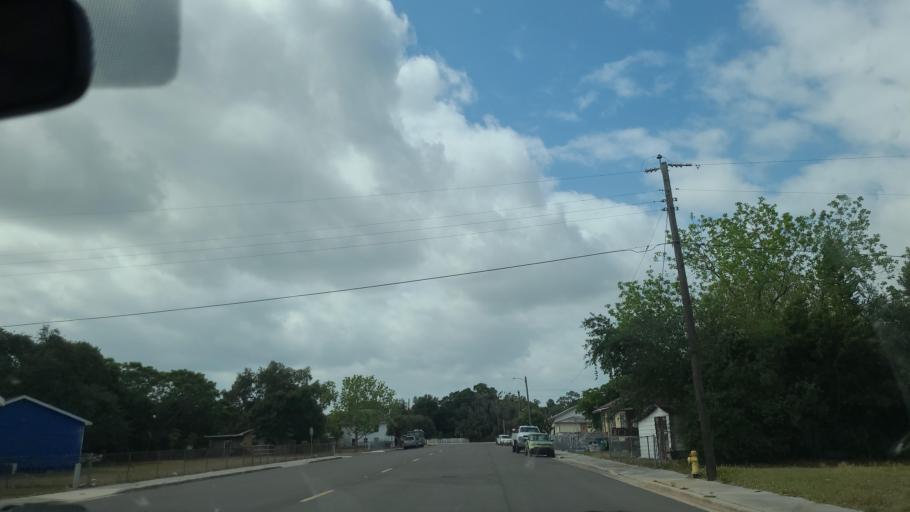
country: US
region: Florida
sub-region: Okeechobee County
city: Okeechobee
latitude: 27.2419
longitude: -80.8276
